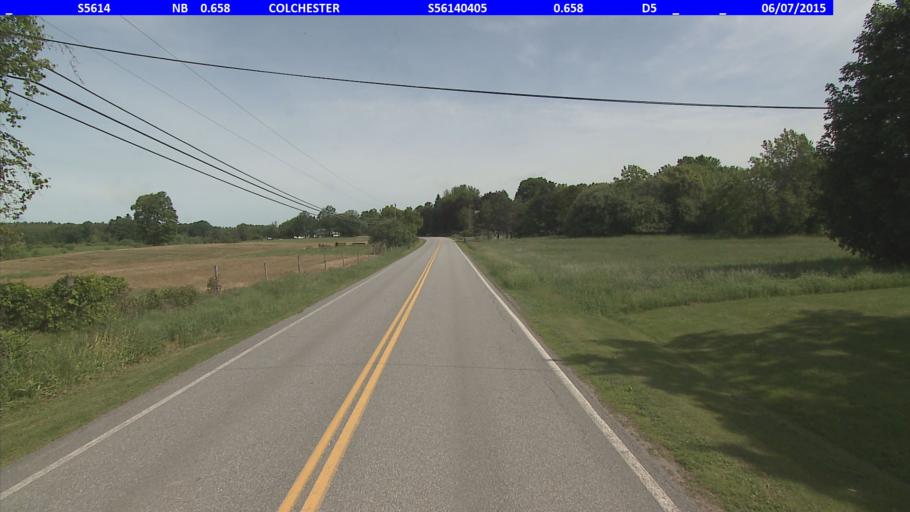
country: US
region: Vermont
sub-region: Chittenden County
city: Colchester
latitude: 44.5320
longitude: -73.1517
